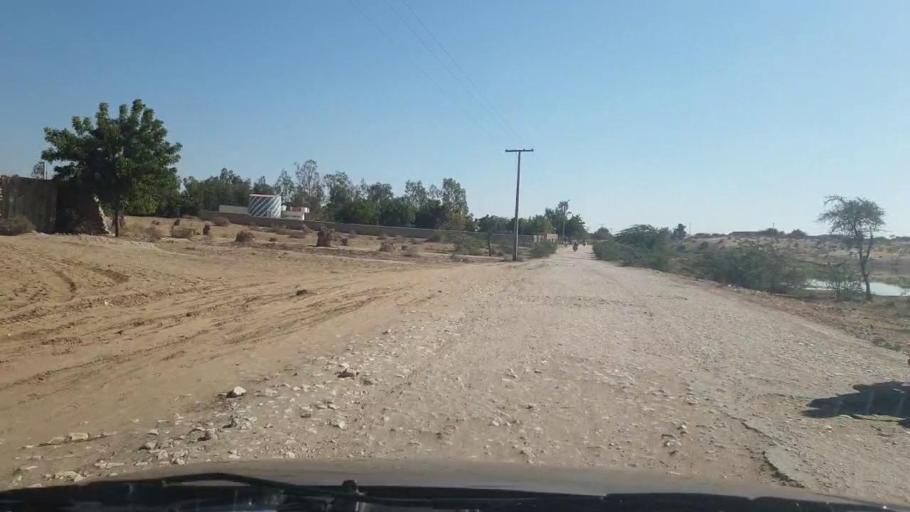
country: PK
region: Sindh
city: Bozdar
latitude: 27.0632
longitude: 68.6244
